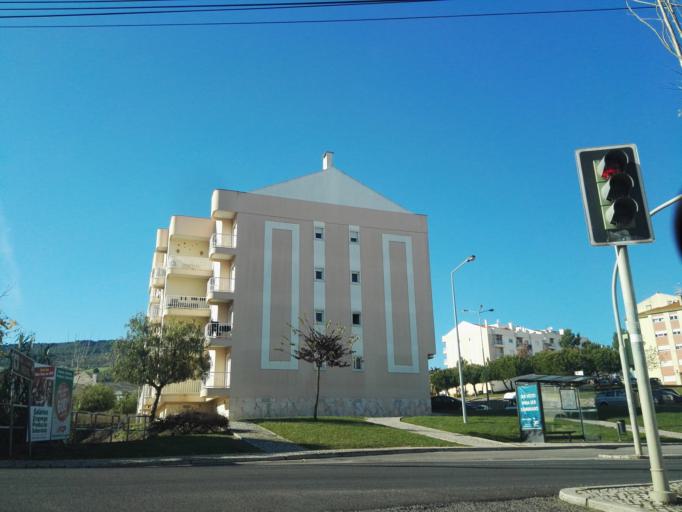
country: PT
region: Lisbon
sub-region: Arruda Dos Vinhos
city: Arruda dos Vinhos
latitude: 38.9867
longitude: -9.0786
